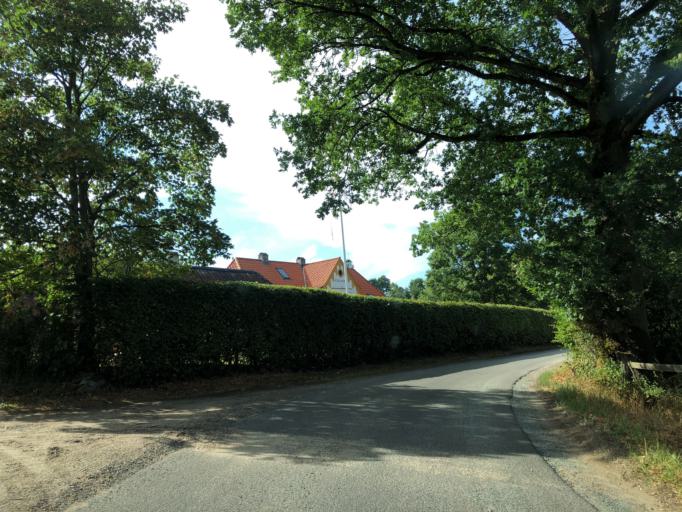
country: DK
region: South Denmark
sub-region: Vejle Kommune
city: Egtved
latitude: 55.6536
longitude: 9.3033
